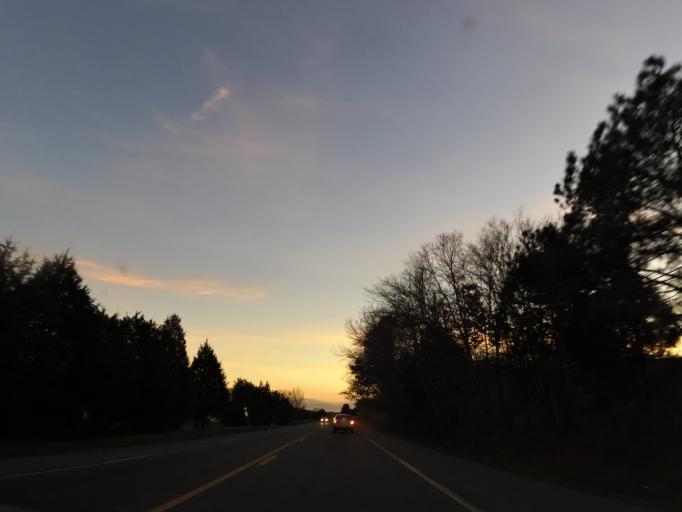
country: US
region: Tennessee
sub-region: Bradley County
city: Wildwood Lake
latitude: 35.0718
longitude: -84.8937
